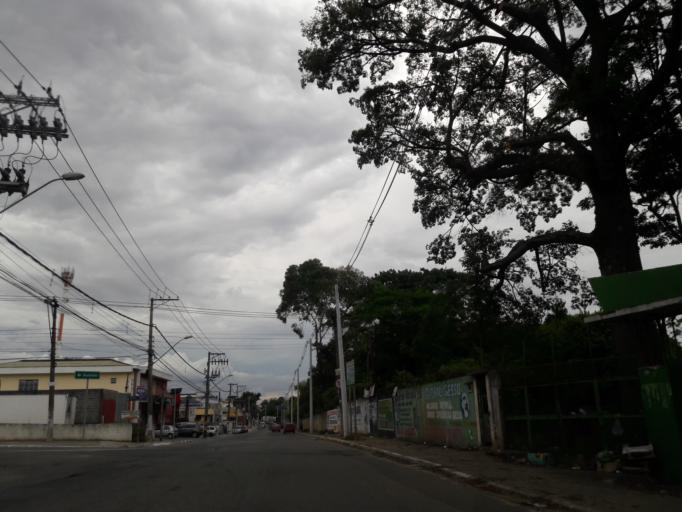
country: BR
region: Sao Paulo
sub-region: Aruja
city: Aruja
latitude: -23.4051
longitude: -46.4071
